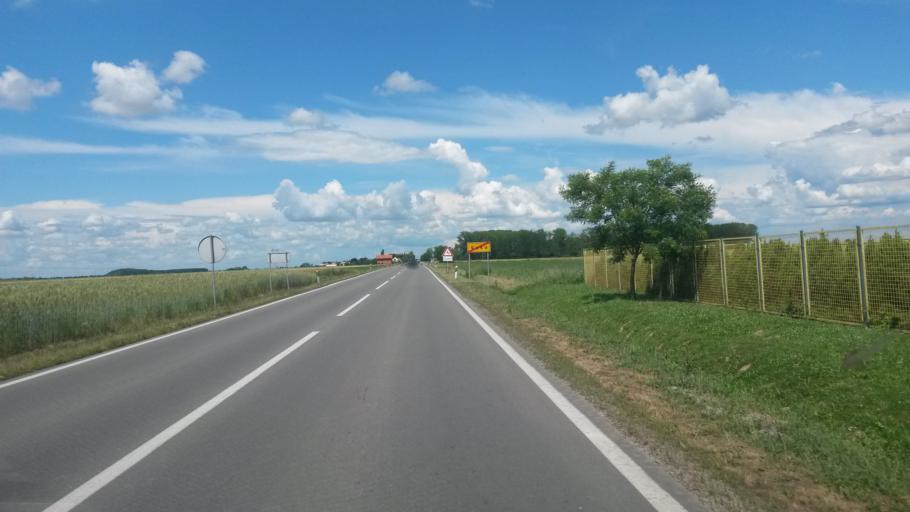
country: HR
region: Osjecko-Baranjska
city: Vuka
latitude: 45.4479
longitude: 18.5077
